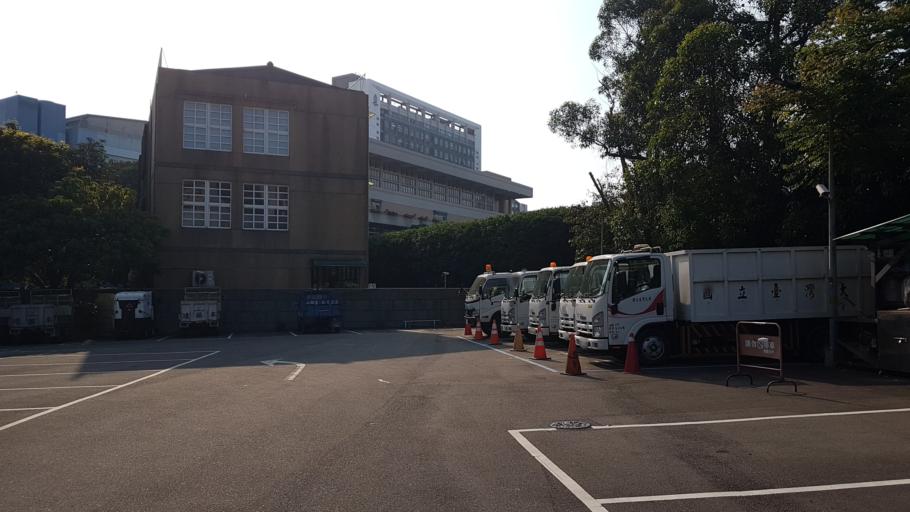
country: TW
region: Taipei
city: Taipei
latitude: 25.0138
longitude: 121.5368
